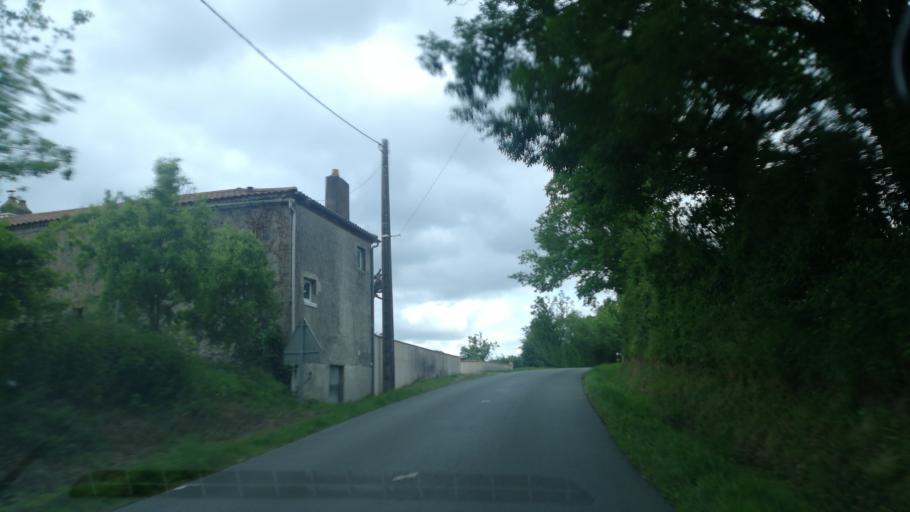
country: FR
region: Poitou-Charentes
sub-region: Departement des Deux-Sevres
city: La Chapelle-Saint-Laurent
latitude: 46.7529
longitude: -0.4934
